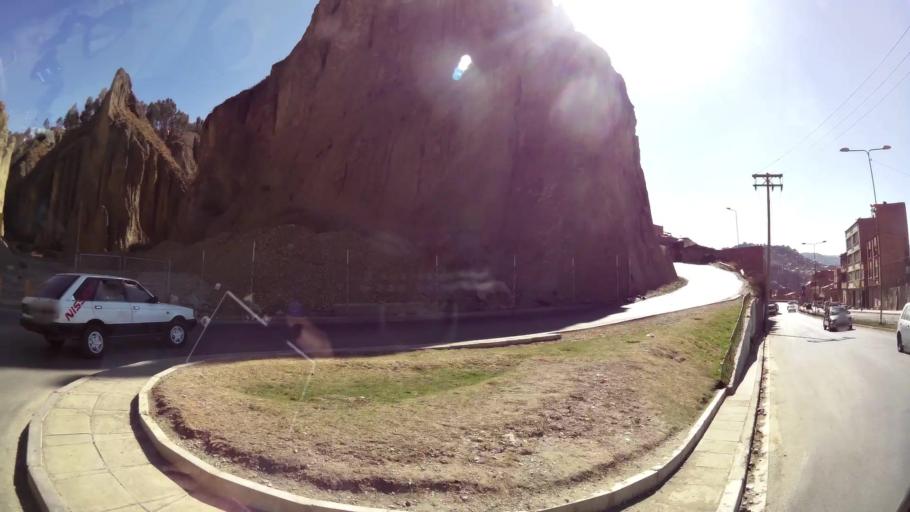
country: BO
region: La Paz
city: La Paz
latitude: -16.5200
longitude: -68.1395
